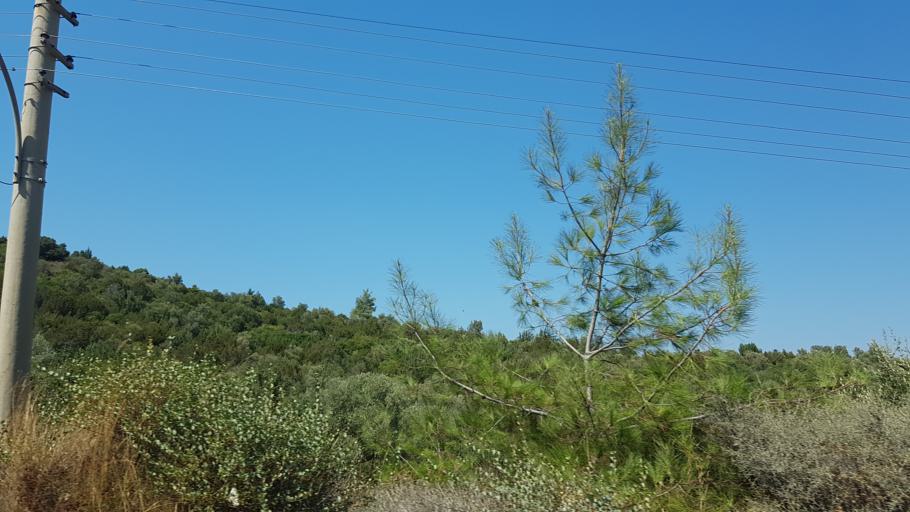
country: TR
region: Mugla
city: Kiulukioi
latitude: 37.1250
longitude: 27.5412
